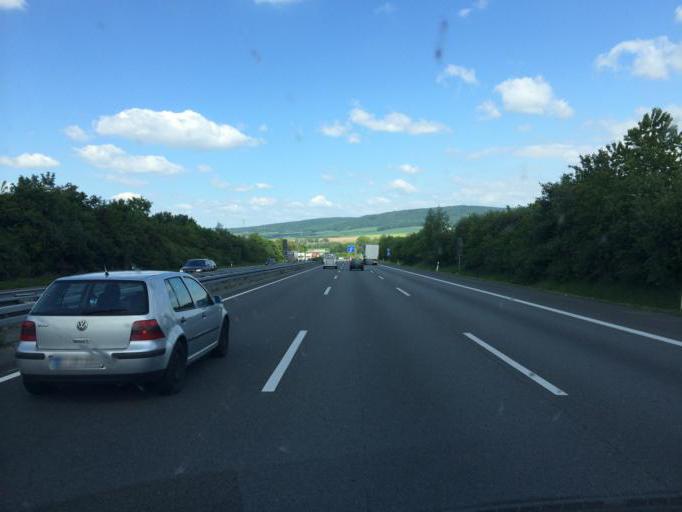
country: DE
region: Lower Saxony
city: Pohle
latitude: 52.2763
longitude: 9.3374
